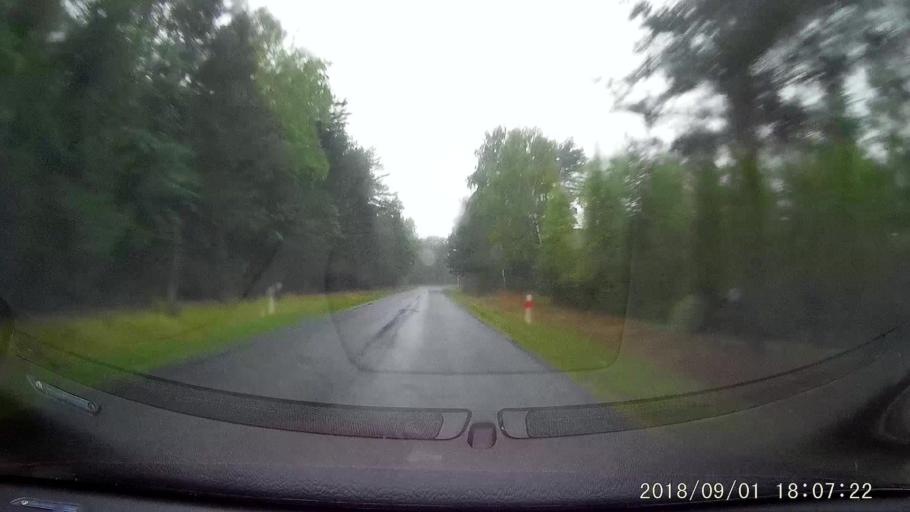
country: PL
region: Lubusz
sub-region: Powiat zaganski
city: Gozdnica
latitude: 51.3516
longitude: 15.1434
